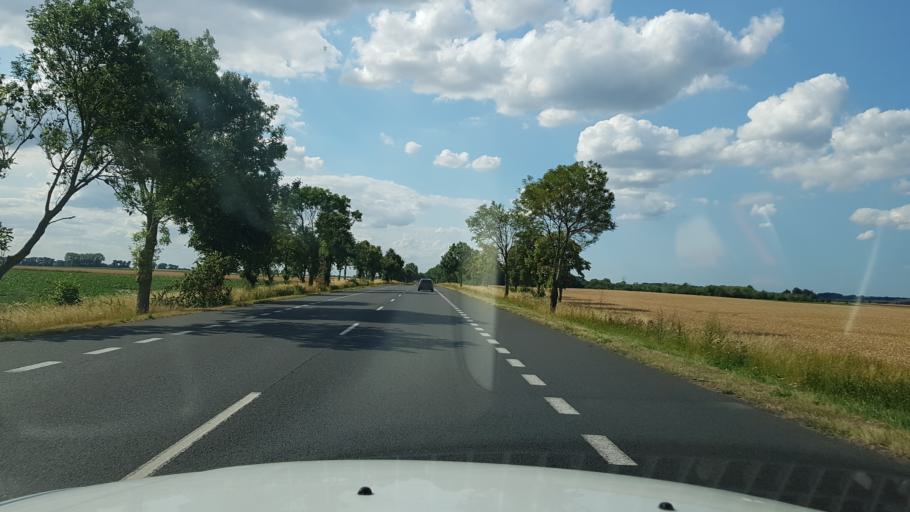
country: PL
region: West Pomeranian Voivodeship
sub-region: Powiat pyrzycki
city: Pyrzyce
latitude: 53.1613
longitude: 14.8693
